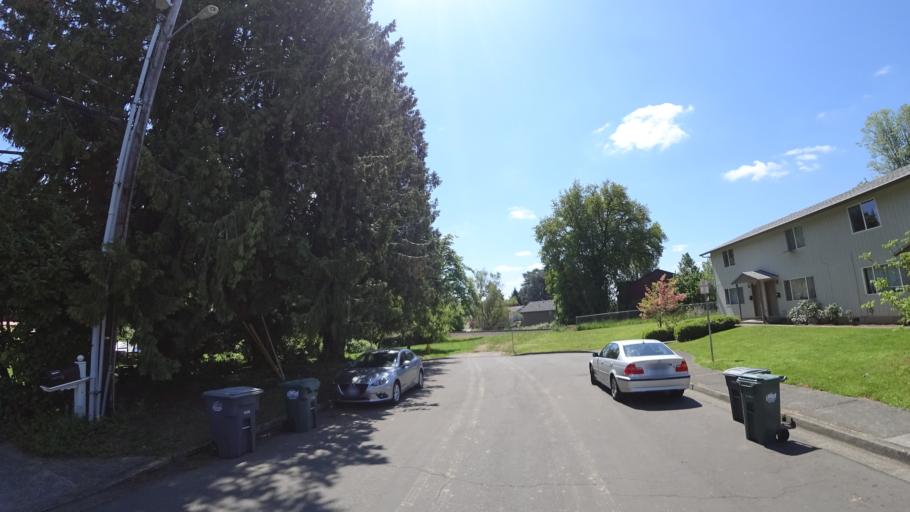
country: US
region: Oregon
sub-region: Washington County
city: Hillsboro
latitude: 45.5153
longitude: -122.9809
